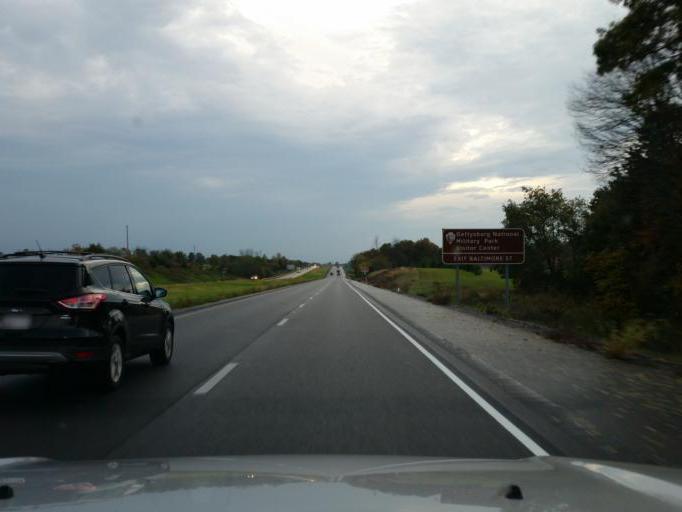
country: US
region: Pennsylvania
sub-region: Adams County
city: Gettysburg
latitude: 39.8808
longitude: -77.1875
